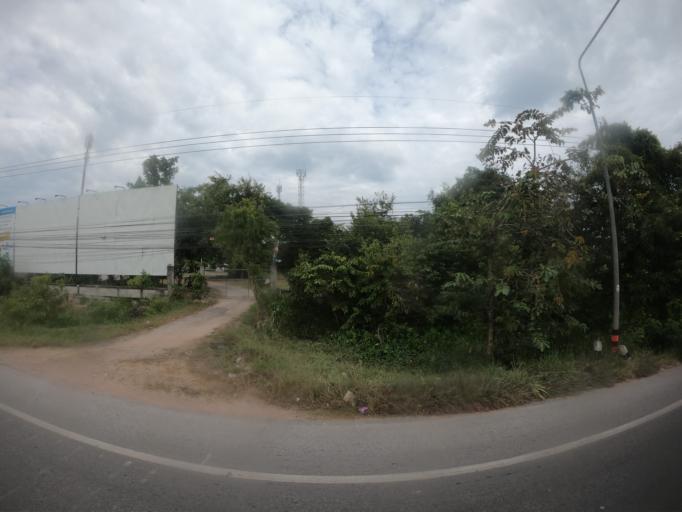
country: TH
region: Maha Sarakham
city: Maha Sarakham
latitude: 16.1648
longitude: 103.3362
